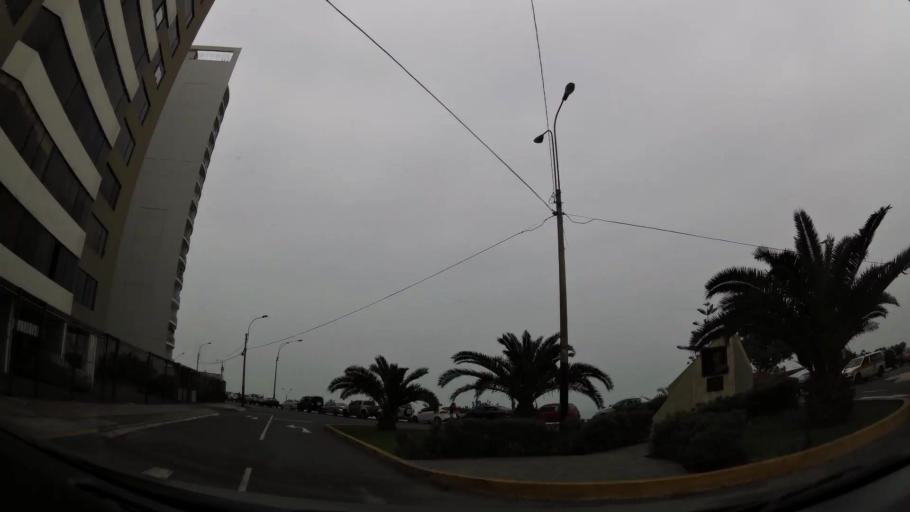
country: PE
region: Lima
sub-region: Lima
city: San Isidro
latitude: -12.1201
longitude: -77.0433
